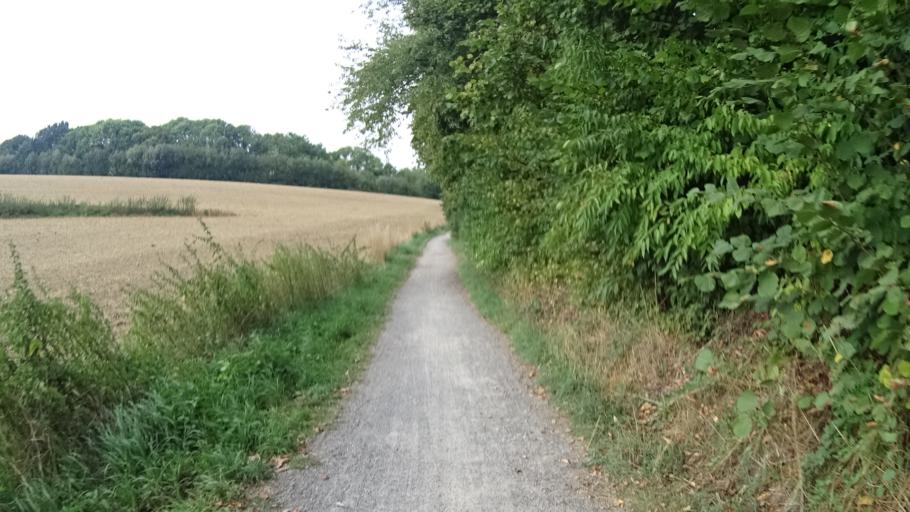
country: DE
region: North Rhine-Westphalia
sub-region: Regierungsbezirk Arnsberg
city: Dortmund
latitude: 51.4880
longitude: 7.4323
